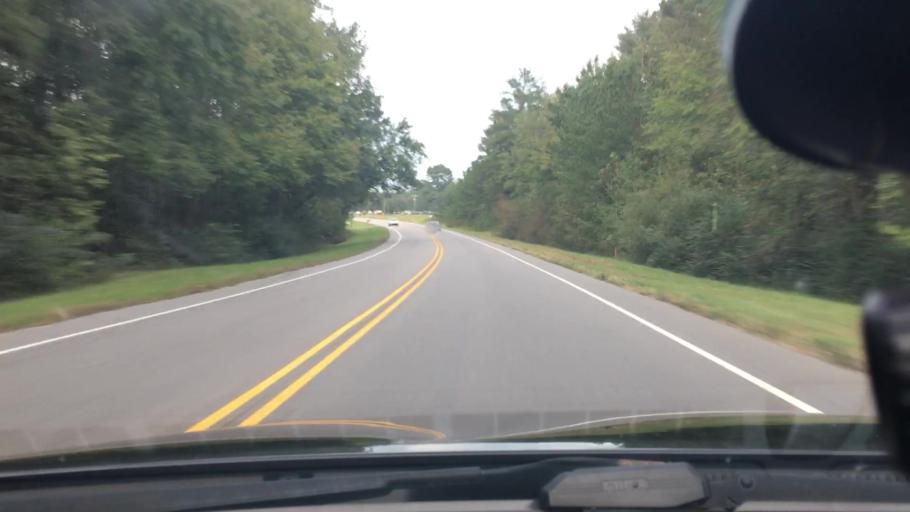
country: US
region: North Carolina
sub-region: Lee County
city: Sanford
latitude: 35.3924
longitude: -79.2471
